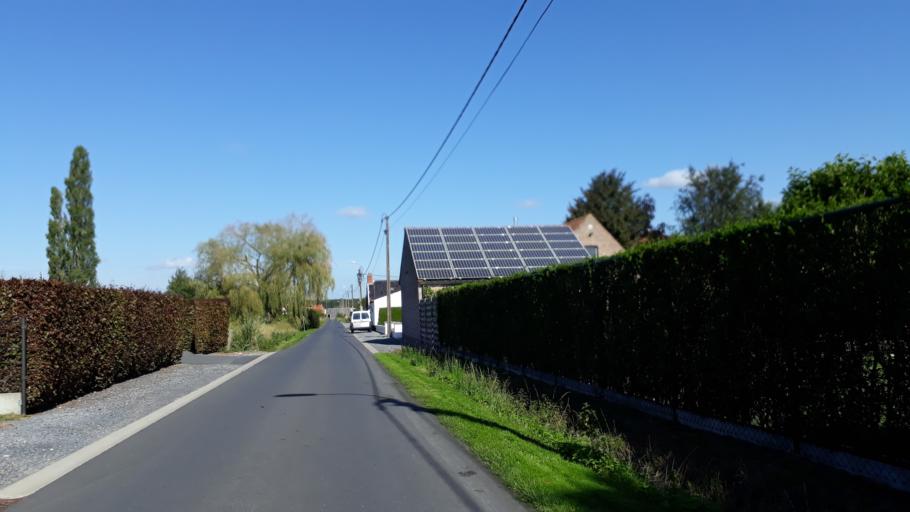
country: BE
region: Flanders
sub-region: Provincie West-Vlaanderen
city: Torhout
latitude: 51.0819
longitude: 3.1029
